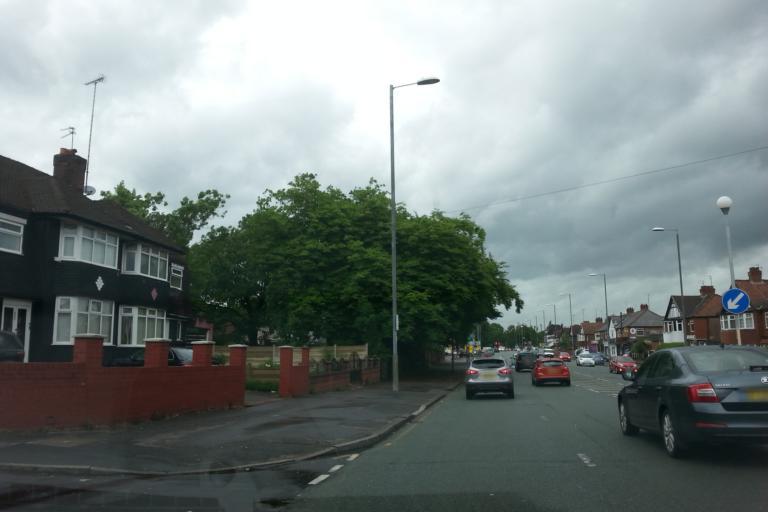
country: GB
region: England
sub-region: Manchester
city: Crumpsall
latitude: 53.5267
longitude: -2.2477
